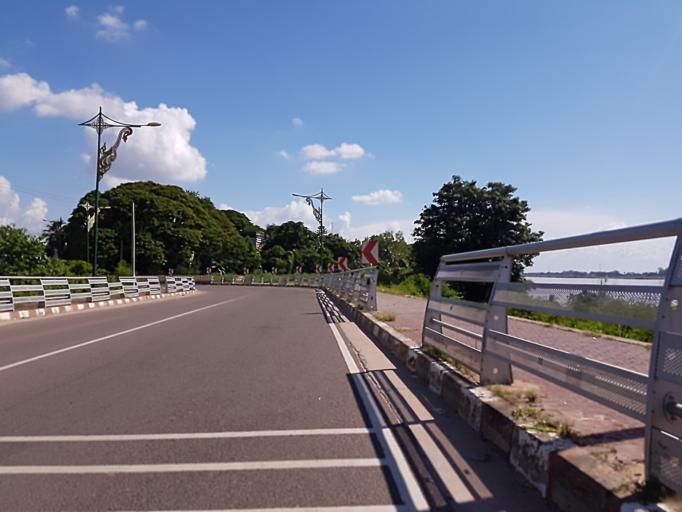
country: LA
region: Vientiane
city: Vientiane
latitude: 17.9403
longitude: 102.6172
